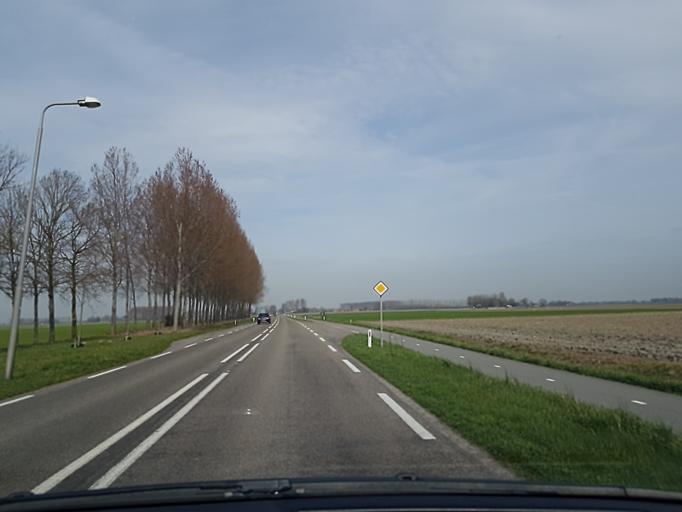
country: NL
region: Zeeland
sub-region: Gemeente Hulst
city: Hulst
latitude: 51.3208
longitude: 4.0328
